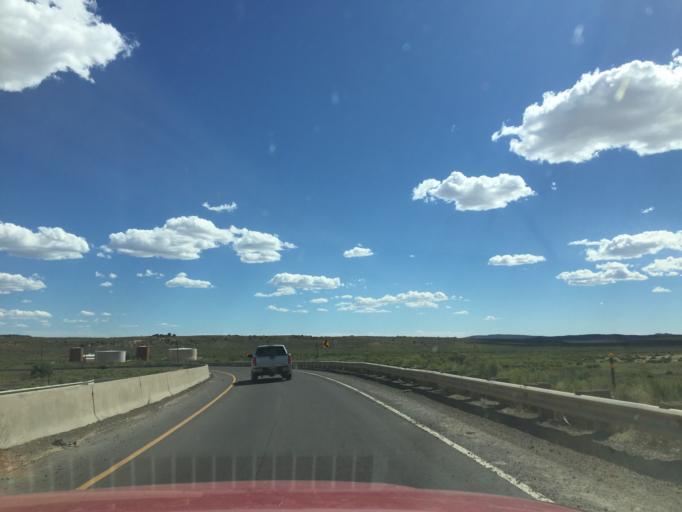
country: US
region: New Mexico
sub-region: McKinley County
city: Twin Lakes
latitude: 35.6276
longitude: -108.7823
